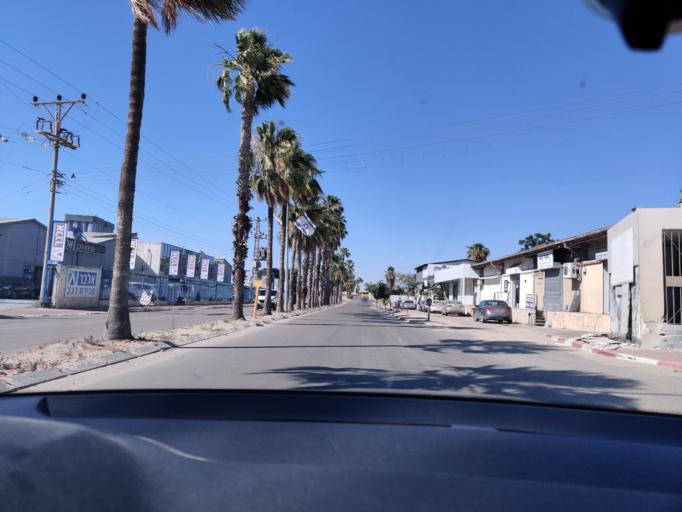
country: IL
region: Southern District
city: Qiryat Gat
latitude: 31.5997
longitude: 34.7791
